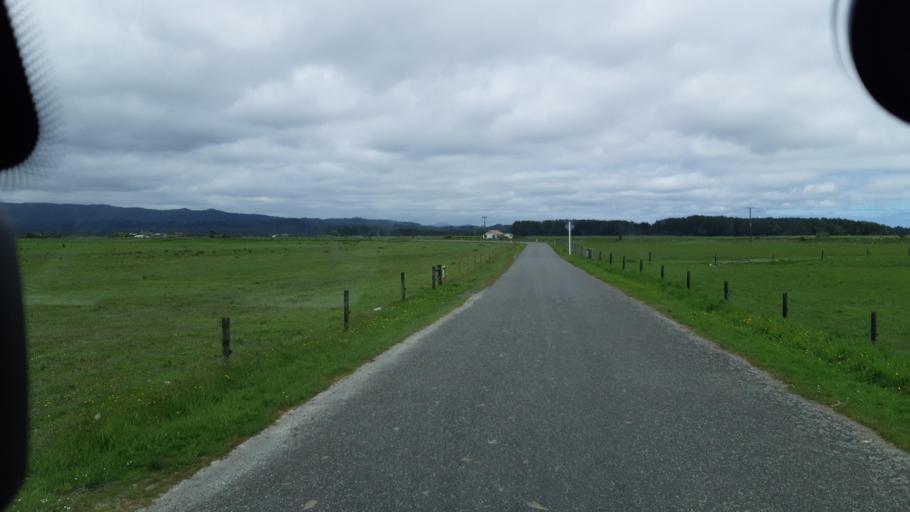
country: NZ
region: West Coast
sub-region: Westland District
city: Hokitika
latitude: -42.6743
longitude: 171.0247
